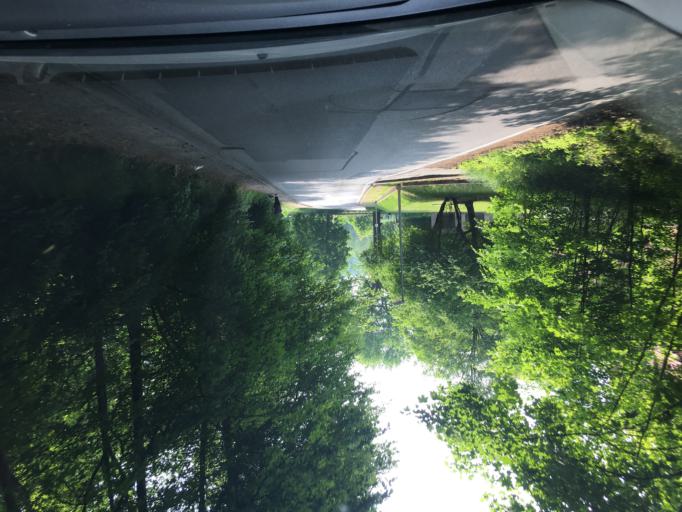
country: DE
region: Saxony
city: Colditz
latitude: 51.1236
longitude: 12.8062
